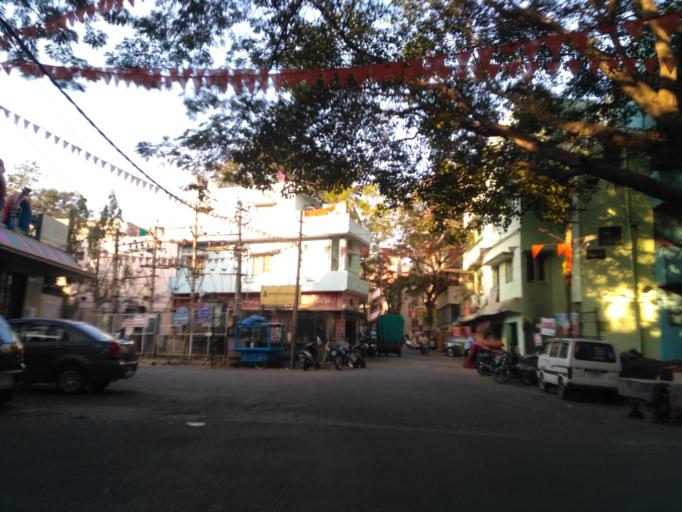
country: IN
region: Karnataka
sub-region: Bangalore Urban
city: Bangalore
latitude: 12.9679
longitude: 77.5416
